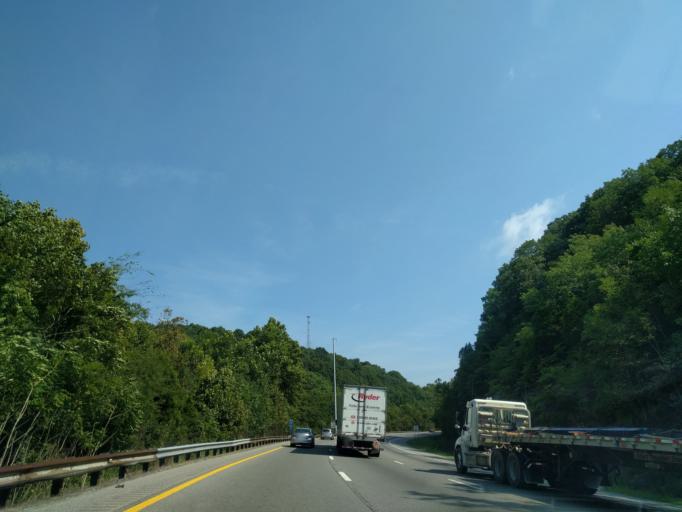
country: US
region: Tennessee
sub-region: Sumner County
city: Millersville
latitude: 36.4103
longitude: -86.7212
